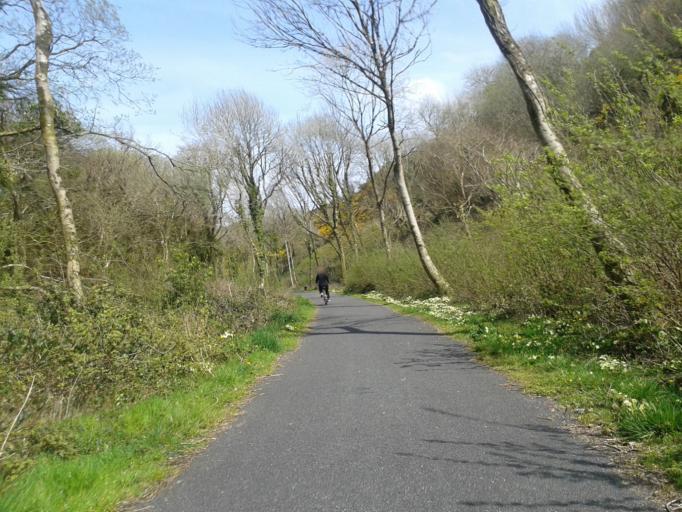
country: GB
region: England
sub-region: Devon
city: Ilfracombe
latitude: 51.1829
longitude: -4.1436
